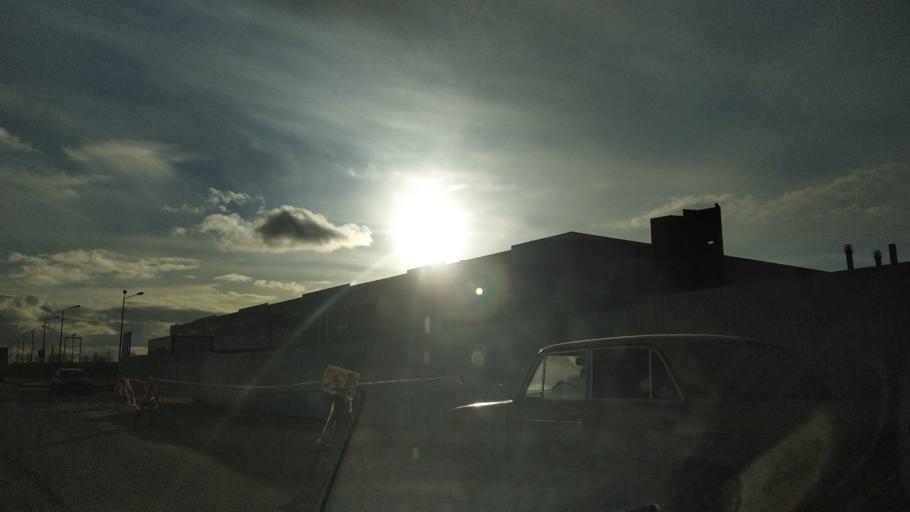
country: RU
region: St.-Petersburg
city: Petro-Slavyanka
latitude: 59.7755
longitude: 30.4605
